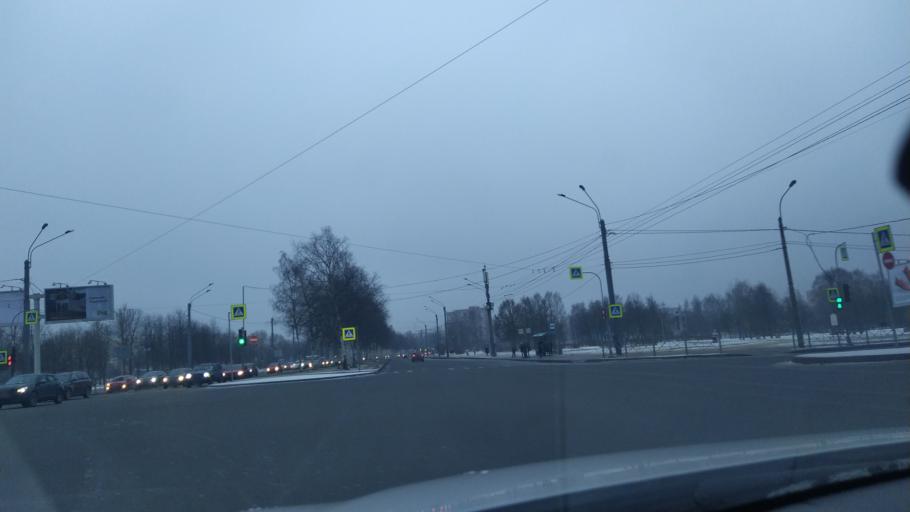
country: RU
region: St.-Petersburg
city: Grazhdanka
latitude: 60.0312
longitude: 30.3917
